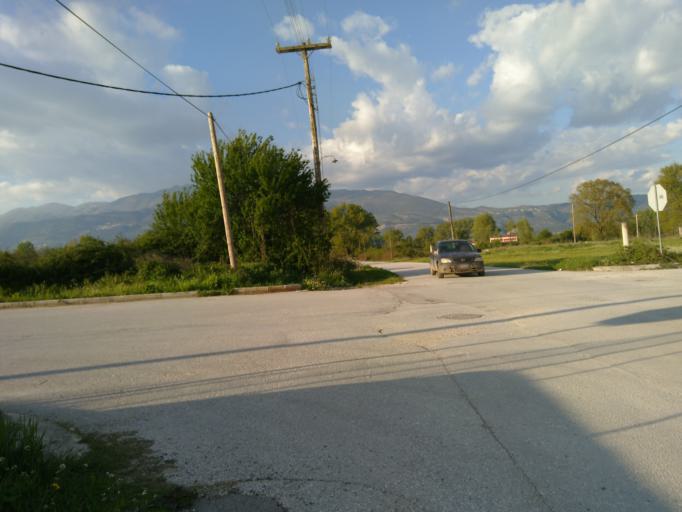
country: GR
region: Epirus
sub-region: Nomos Ioanninon
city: Katsikas
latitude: 39.6260
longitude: 20.8879
